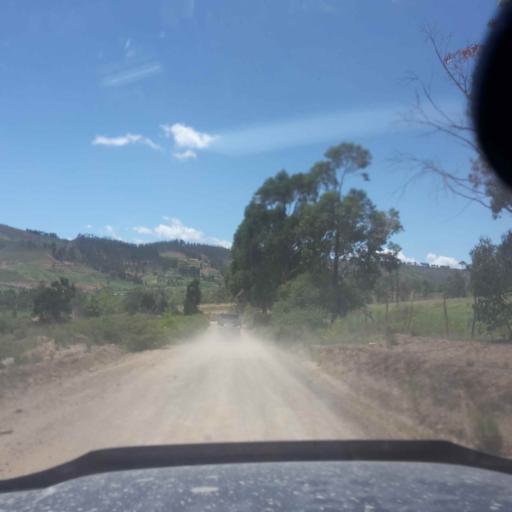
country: BO
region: Cochabamba
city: Totora
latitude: -17.7646
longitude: -65.2359
